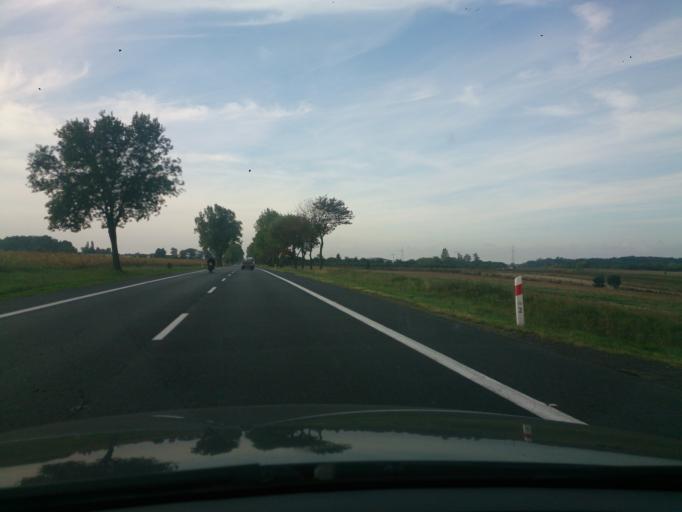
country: PL
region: Kujawsko-Pomorskie
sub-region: Powiat swiecki
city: Pruszcz
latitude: 53.3246
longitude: 18.2831
